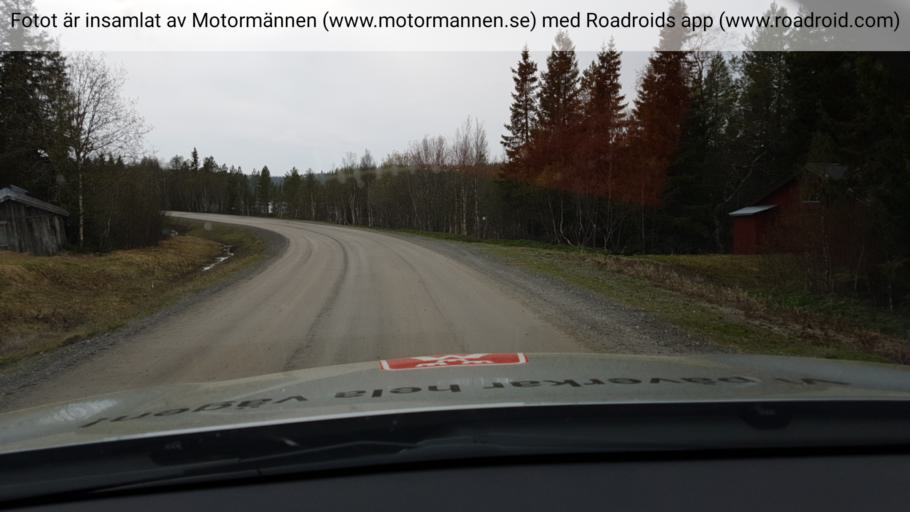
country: NO
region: Nord-Trondelag
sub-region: Snasa
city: Snaase
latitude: 63.7078
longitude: 12.3520
